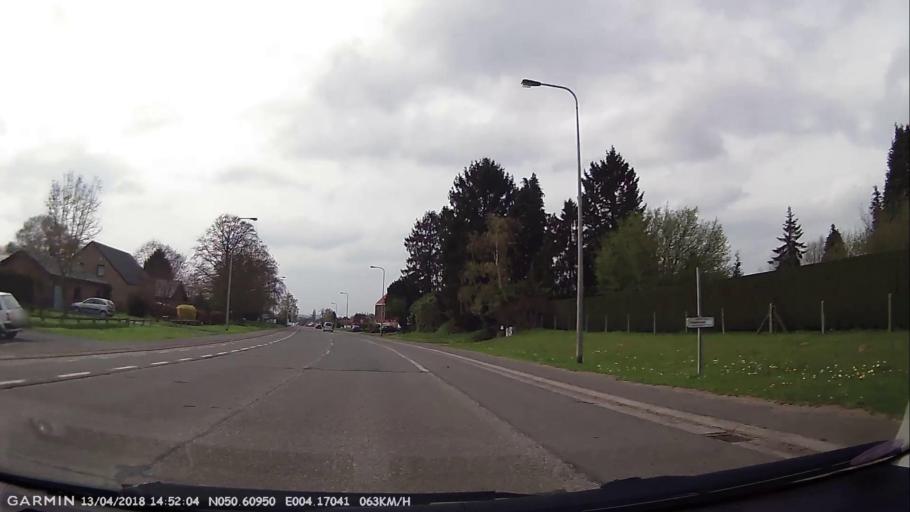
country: BE
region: Wallonia
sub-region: Province du Hainaut
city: Braine-le-Comte
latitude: 50.6097
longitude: 4.1702
